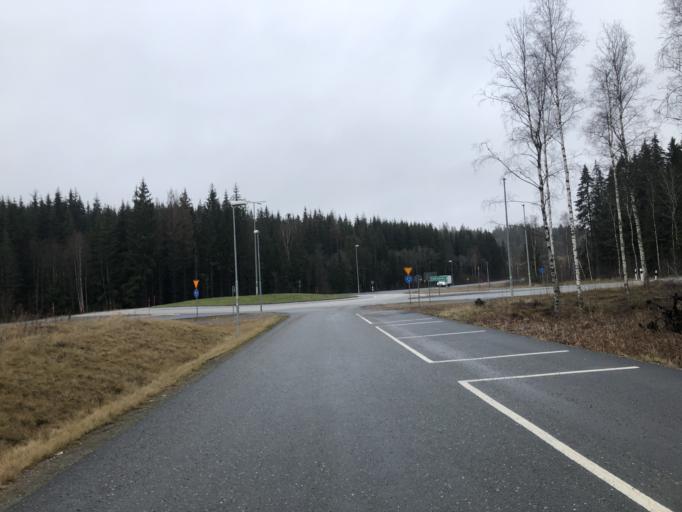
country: SE
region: Vaestra Goetaland
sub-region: Ulricehamns Kommun
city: Ulricehamn
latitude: 57.8199
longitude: 13.2860
